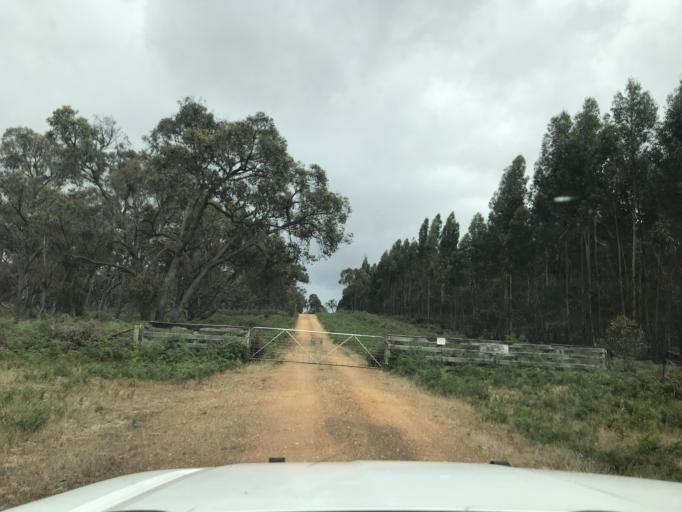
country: AU
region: South Australia
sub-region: Wattle Range
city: Penola
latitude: -37.2928
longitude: 141.2941
